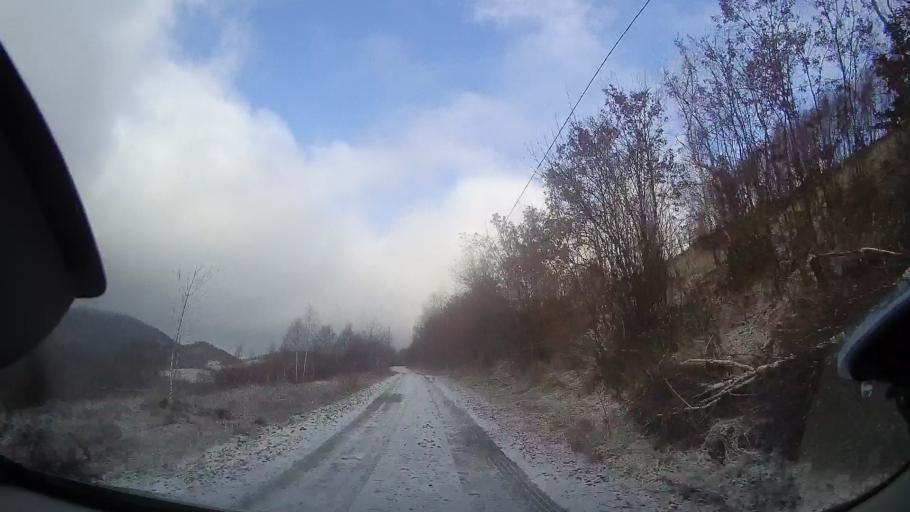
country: RO
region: Cluj
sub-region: Comuna Valea Ierii
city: Valea Ierii
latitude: 46.6521
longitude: 23.3539
